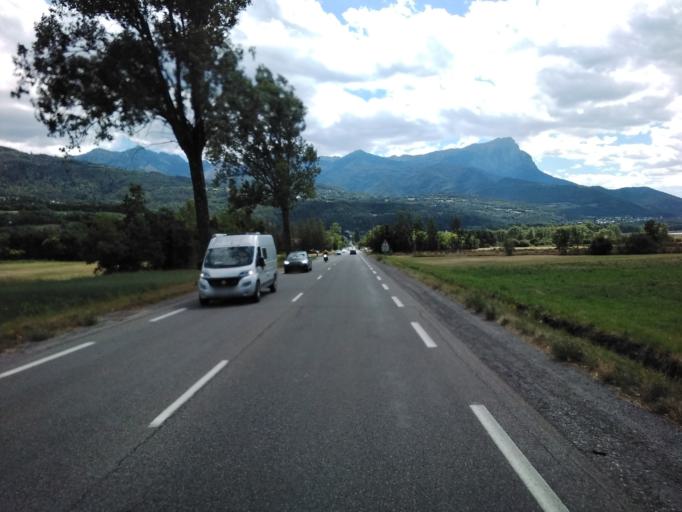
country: FR
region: Provence-Alpes-Cote d'Azur
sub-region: Departement des Hautes-Alpes
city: Embrun
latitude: 44.5446
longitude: 6.4806
